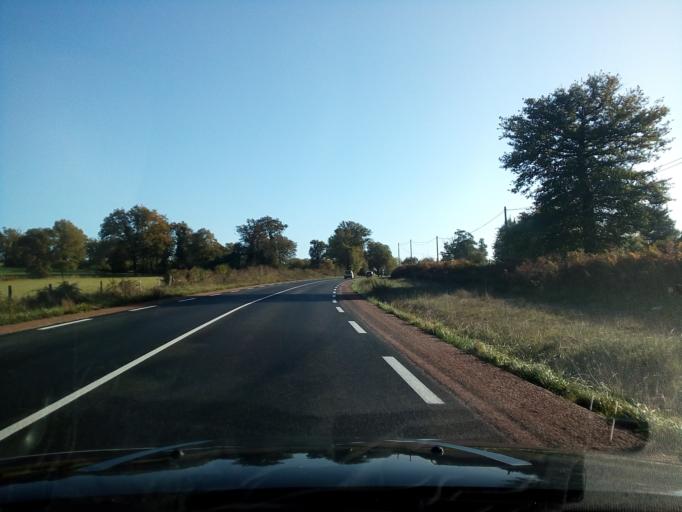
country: FR
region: Limousin
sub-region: Departement de la Haute-Vienne
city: Le Dorat
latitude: 46.1529
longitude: 1.1176
